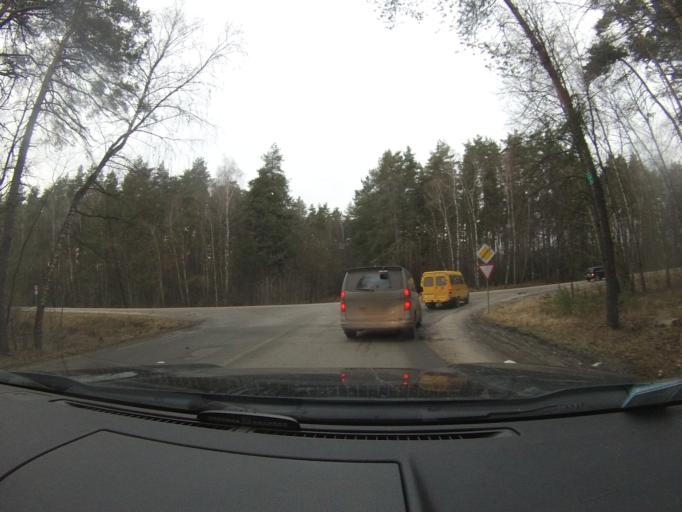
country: RU
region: Moskovskaya
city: Voskresensk
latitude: 55.3377
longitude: 38.6732
